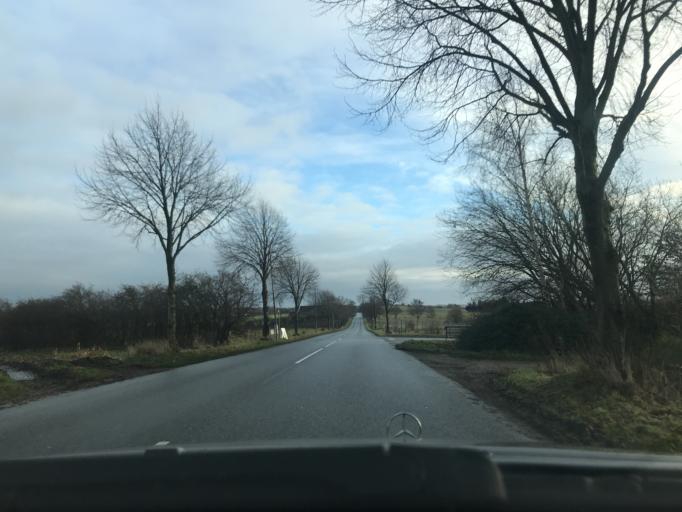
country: DK
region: South Denmark
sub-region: Sonderborg Kommune
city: Broager
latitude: 54.8882
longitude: 9.6869
